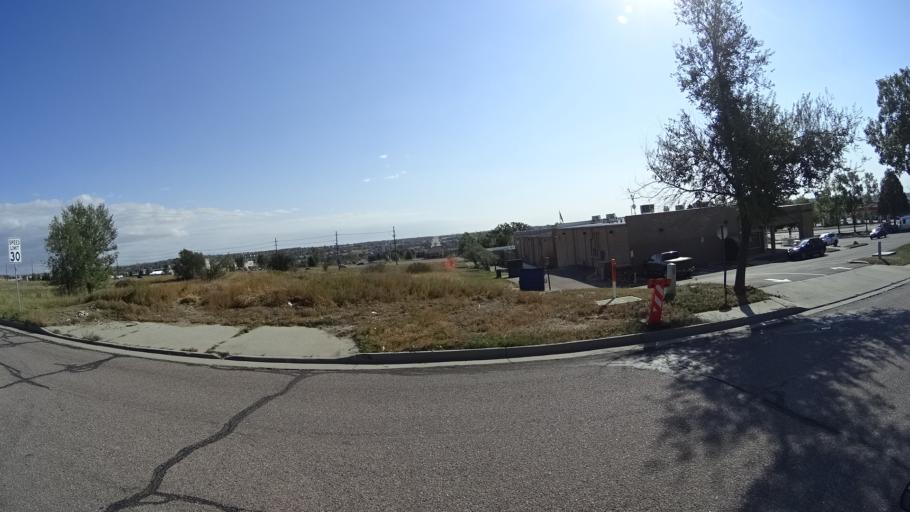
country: US
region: Colorado
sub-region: El Paso County
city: Cimarron Hills
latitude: 38.8864
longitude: -104.7224
